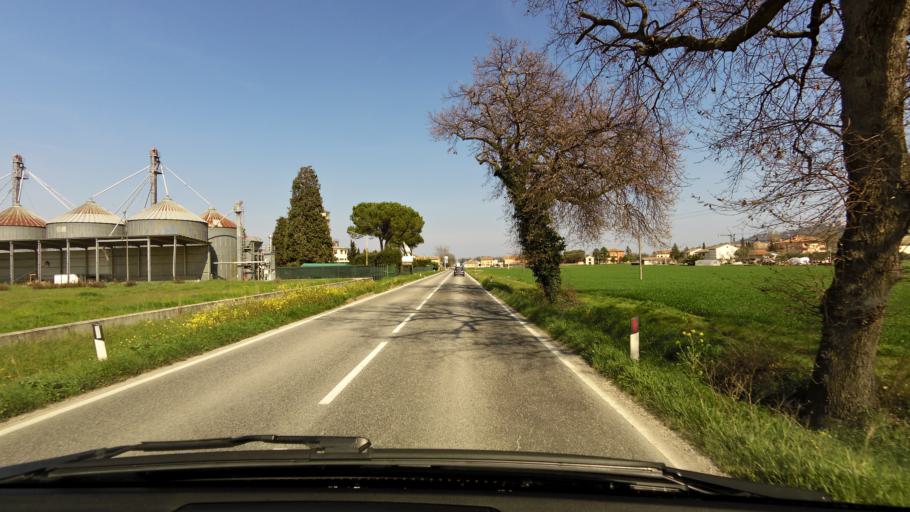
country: IT
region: The Marches
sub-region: Provincia di Macerata
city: Potenza Picena
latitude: 43.3782
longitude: 13.6038
